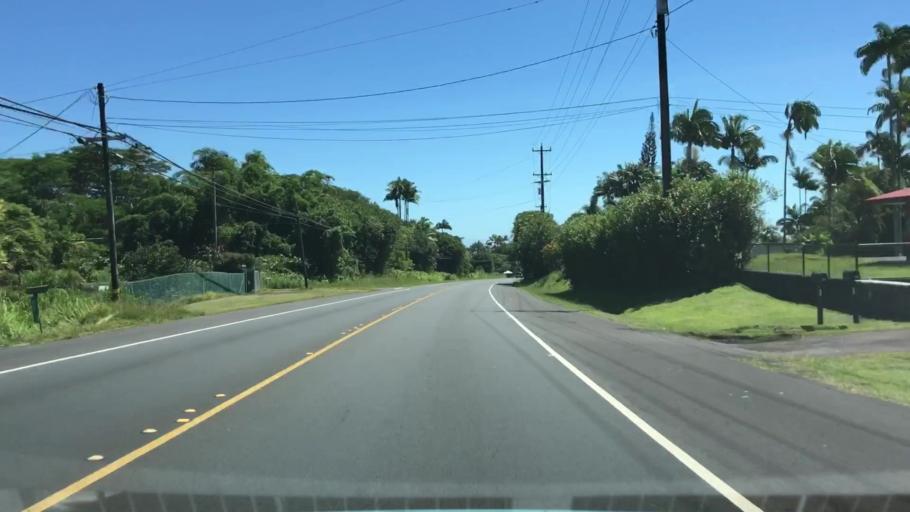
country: US
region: Hawaii
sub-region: Hawaii County
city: Mountain View
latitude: 19.5716
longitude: -155.0774
